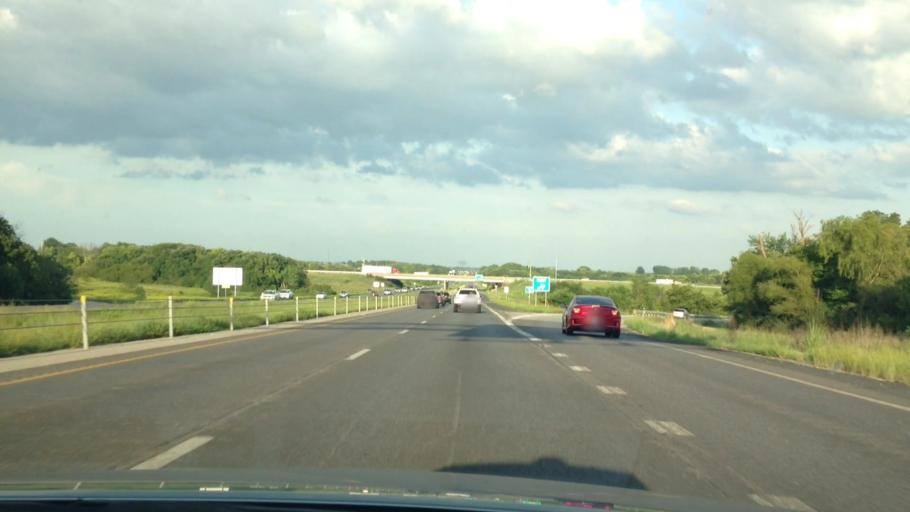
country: US
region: Missouri
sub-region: Clay County
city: Pleasant Valley
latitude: 39.2428
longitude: -94.5139
